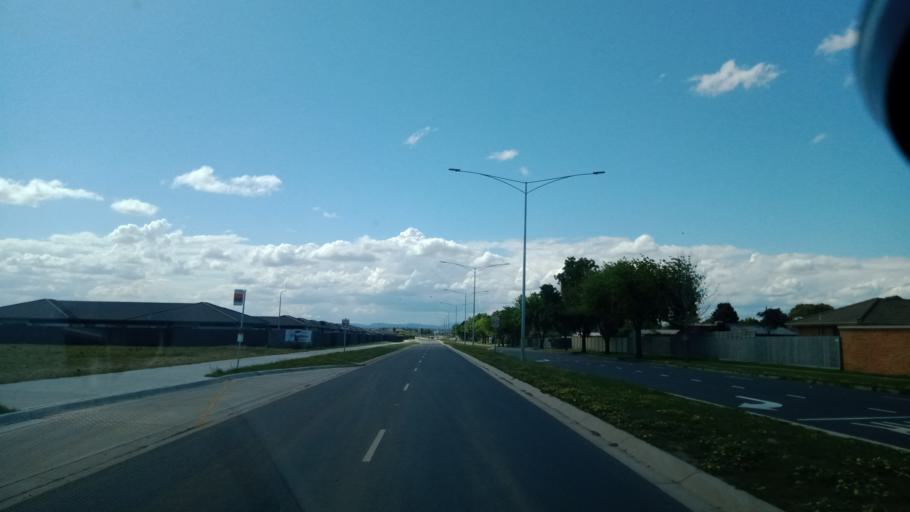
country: AU
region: Victoria
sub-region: Casey
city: Cranbourne West
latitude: -38.1072
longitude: 145.2527
